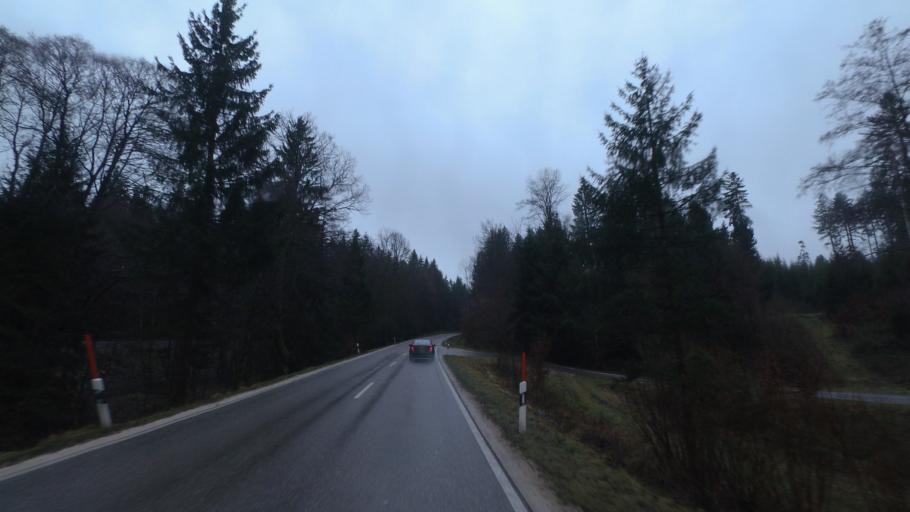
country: DE
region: Bavaria
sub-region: Upper Bavaria
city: Surberg
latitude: 47.8915
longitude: 12.6832
